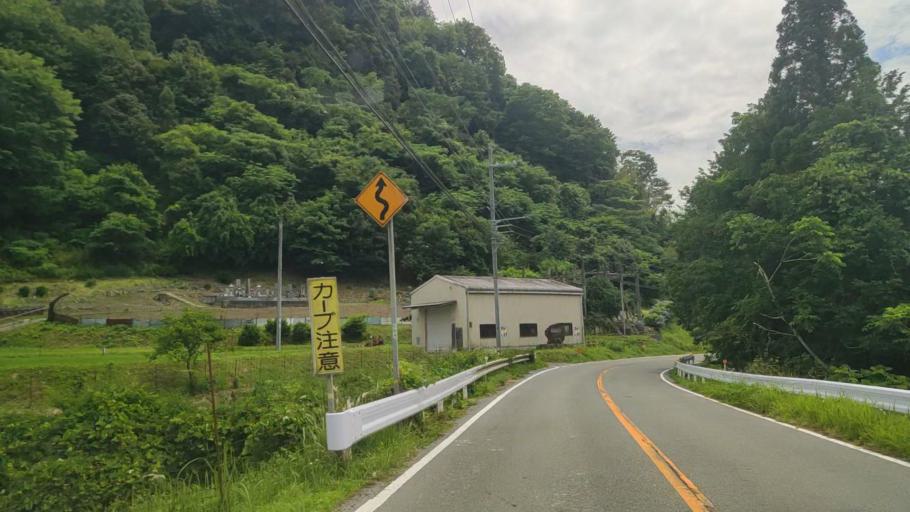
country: JP
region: Hyogo
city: Yamazakicho-nakabirose
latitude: 35.0886
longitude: 134.3607
